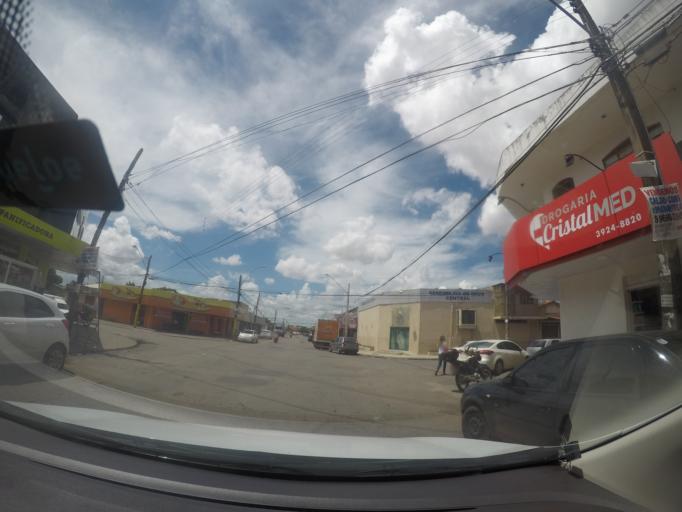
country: BR
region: Goias
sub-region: Goiania
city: Goiania
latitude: -16.6770
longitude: -49.3150
